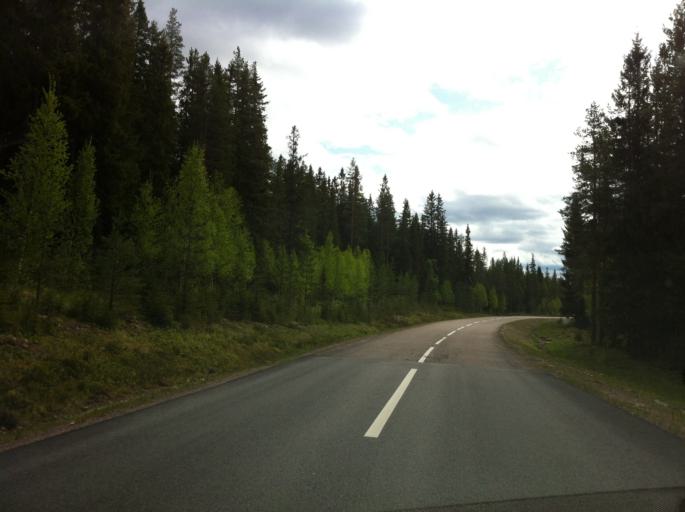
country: NO
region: Hedmark
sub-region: Trysil
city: Innbygda
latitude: 61.5622
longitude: 13.0897
